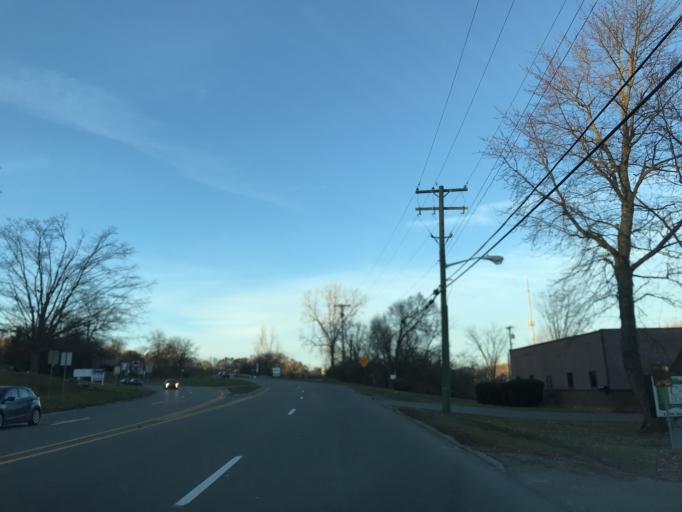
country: US
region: Michigan
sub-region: Washtenaw County
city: Ann Arbor
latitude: 42.2976
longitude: -83.7463
